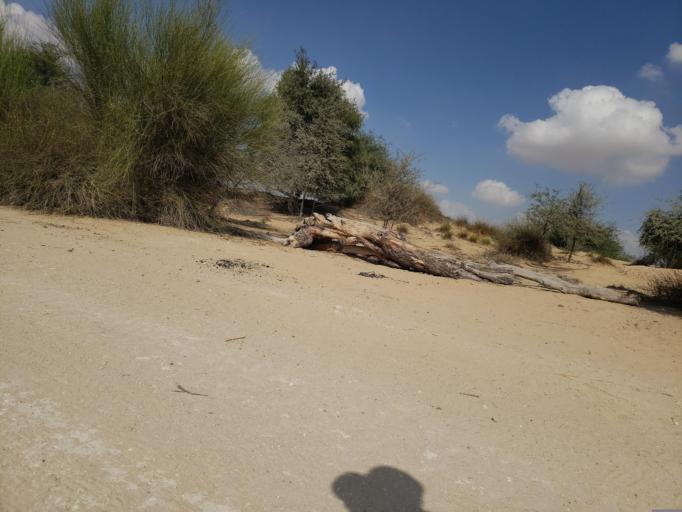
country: AE
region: Dubai
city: Dubai
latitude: 24.8343
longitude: 55.3799
